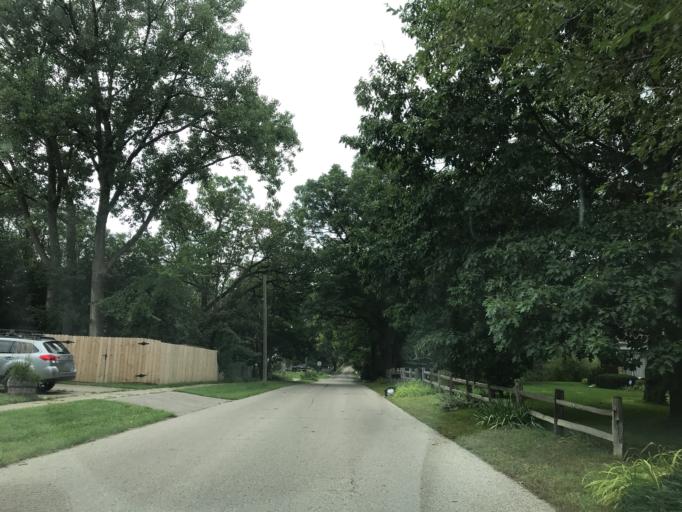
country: US
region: Michigan
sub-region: Washtenaw County
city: Ypsilanti
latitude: 42.2534
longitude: -83.6055
